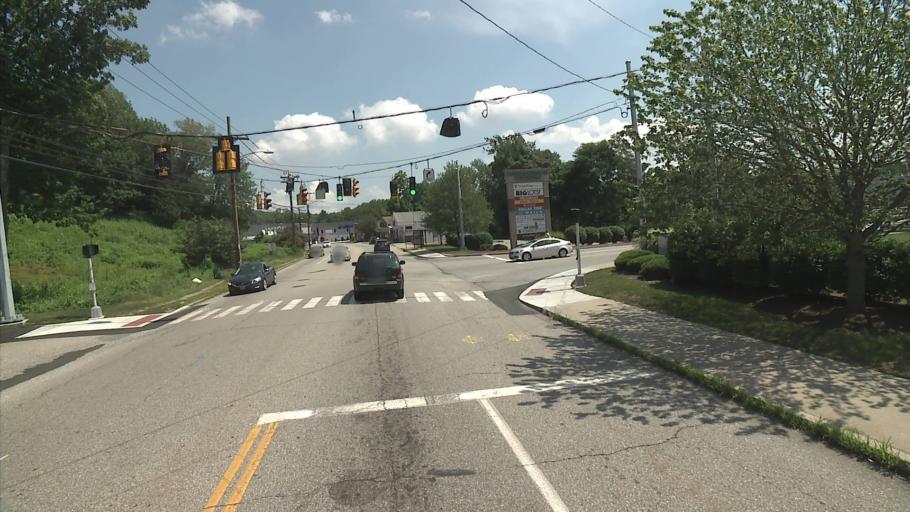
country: US
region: Connecticut
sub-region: New London County
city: Norwich
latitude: 41.5467
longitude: -72.0919
